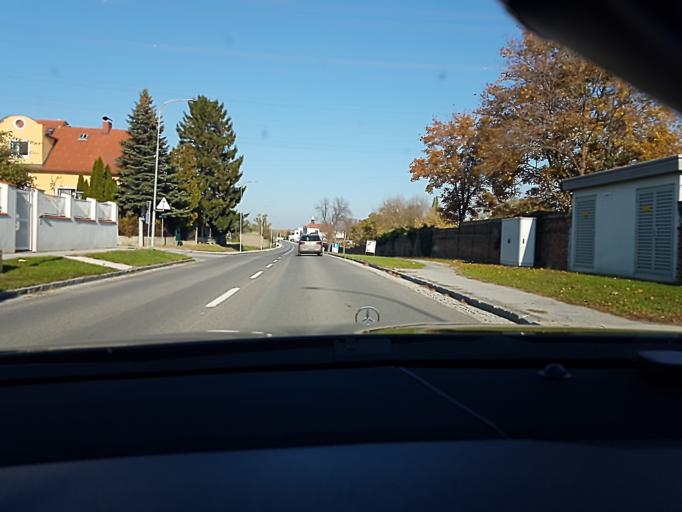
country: AT
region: Lower Austria
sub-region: Politischer Bezirk Wien-Umgebung
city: Lanzendorf
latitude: 48.1026
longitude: 16.4307
